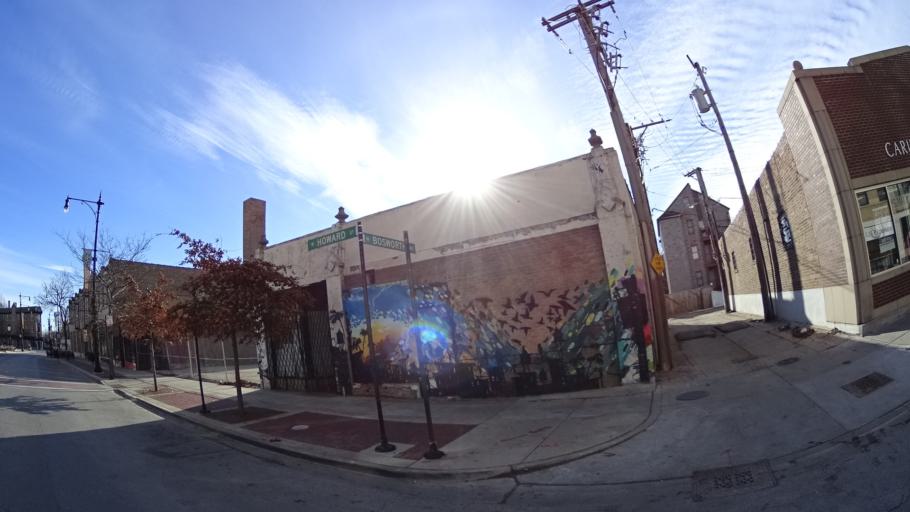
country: US
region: Illinois
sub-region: Cook County
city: Evanston
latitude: 42.0194
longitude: -87.6697
